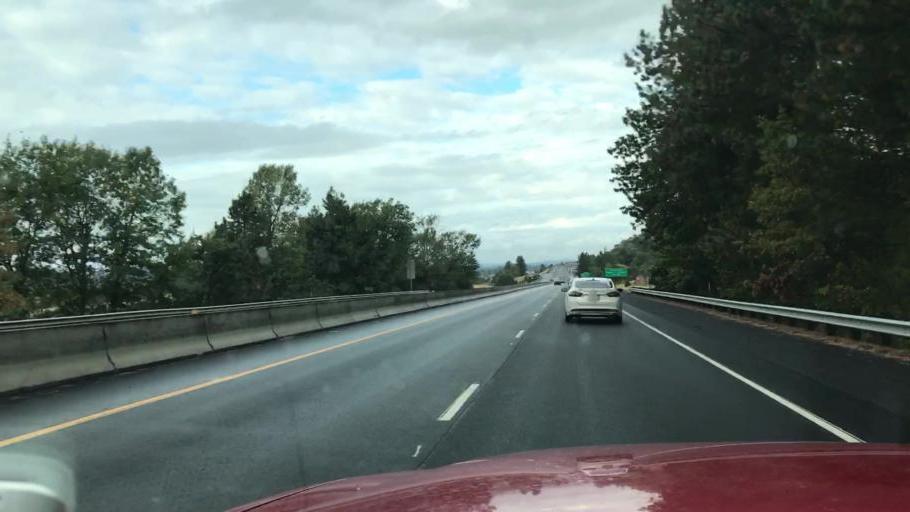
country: US
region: Oregon
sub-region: Josephine County
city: Fruitdale
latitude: 42.4377
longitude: -123.2798
